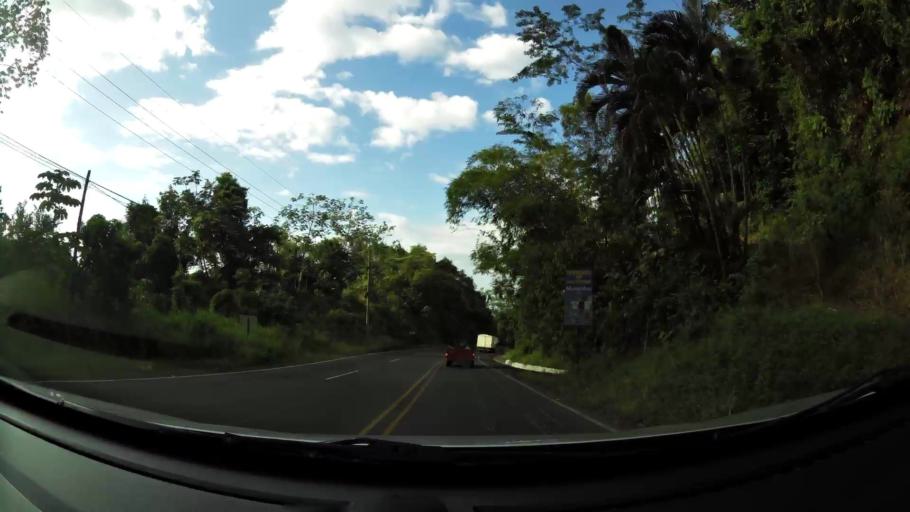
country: CR
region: Puntarenas
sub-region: Canton de Garabito
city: Jaco
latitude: 9.6964
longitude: -84.6403
